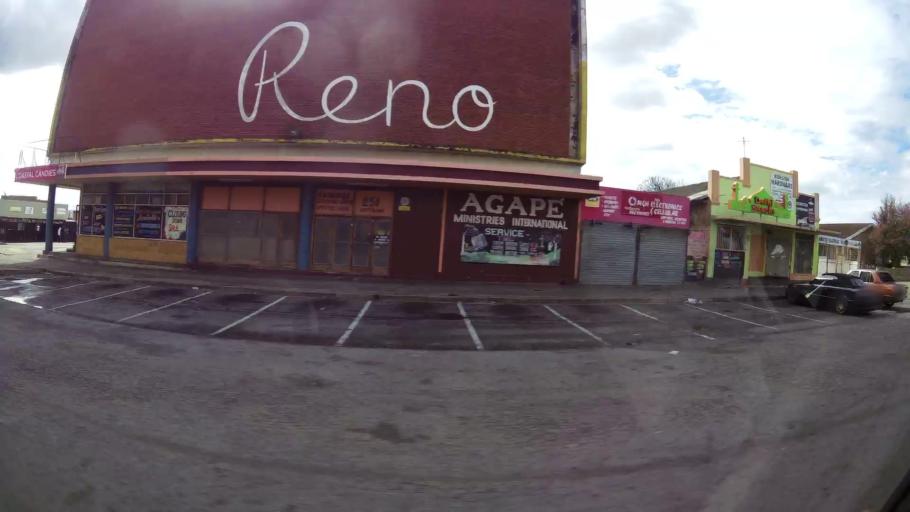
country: ZA
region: Eastern Cape
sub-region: Nelson Mandela Bay Metropolitan Municipality
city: Port Elizabeth
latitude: -33.9281
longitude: 25.5707
